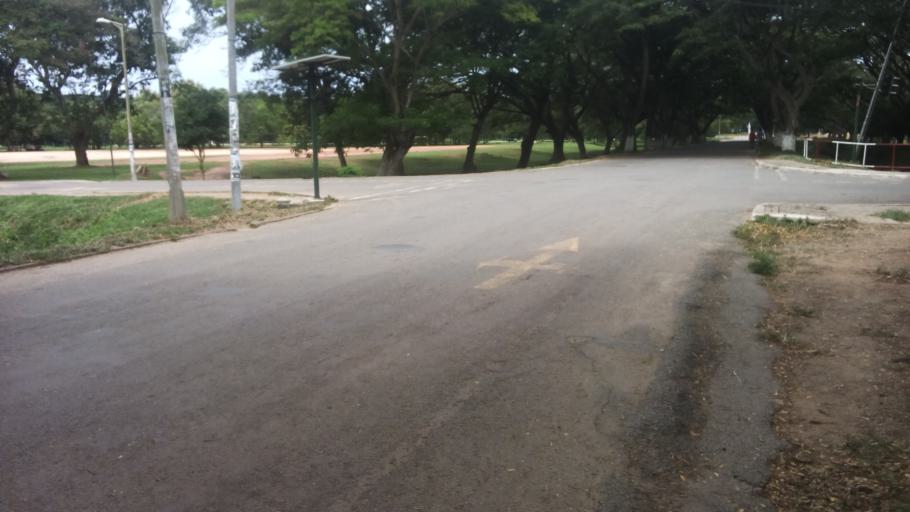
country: GH
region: Central
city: Cape Coast
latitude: 5.1180
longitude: -1.2874
